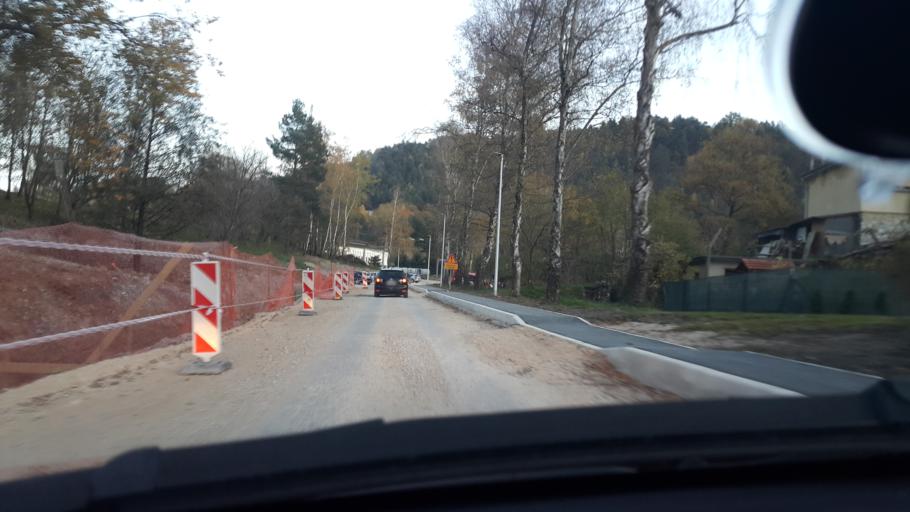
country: SI
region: Celje
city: Celje
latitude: 46.2287
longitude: 15.2805
